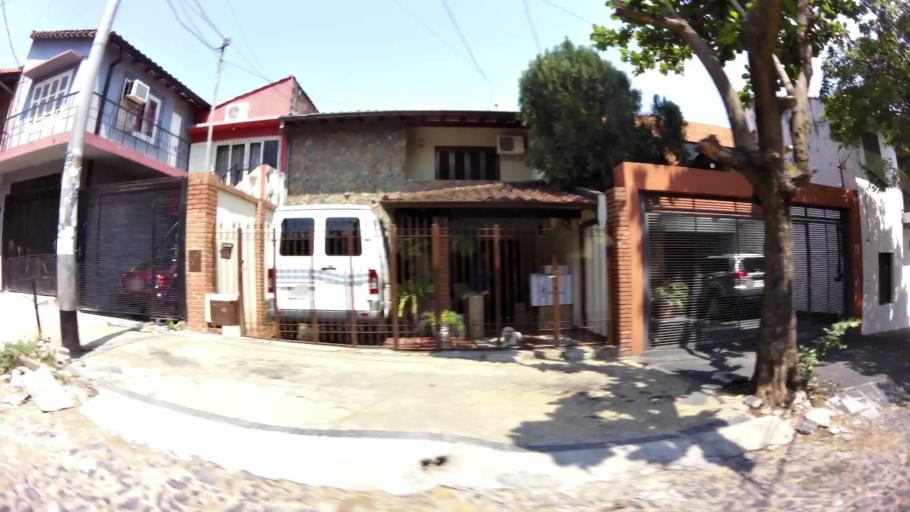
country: PY
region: Presidente Hayes
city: Nanawa
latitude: -25.2829
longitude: -57.6523
